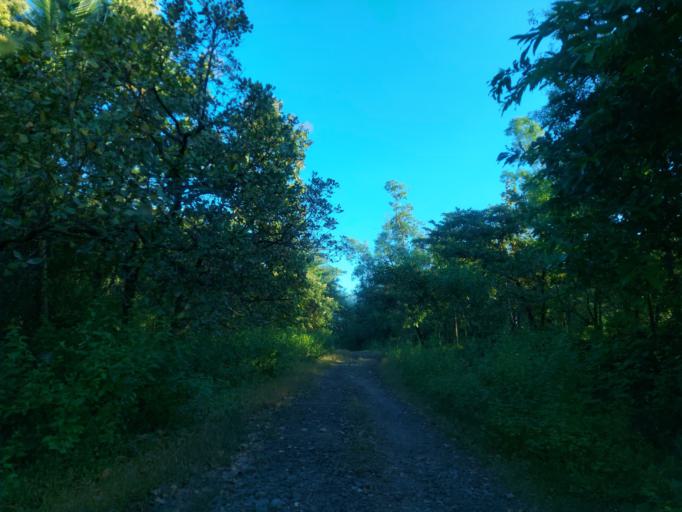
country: IN
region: Maharashtra
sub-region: Sindhudurg
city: Kudal
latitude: 16.0738
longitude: 73.8257
